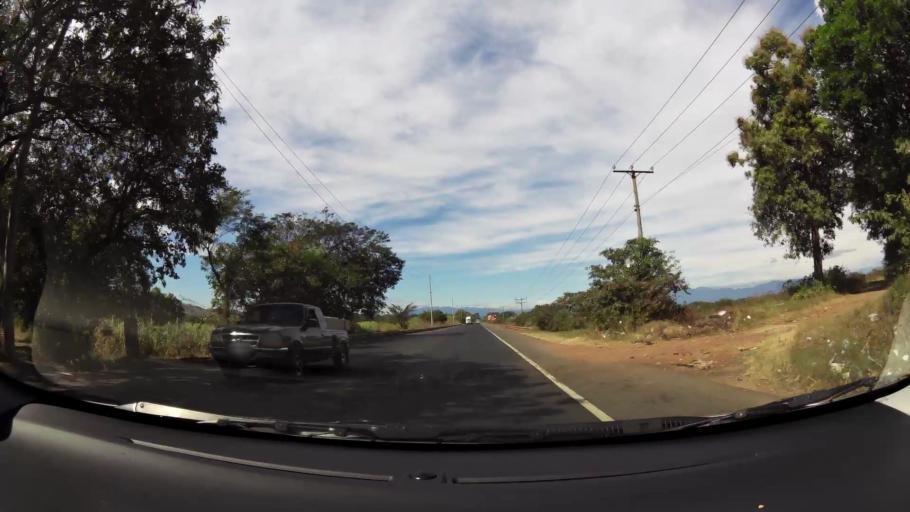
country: SV
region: San Salvador
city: Guazapa
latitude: 13.9061
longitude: -89.1805
